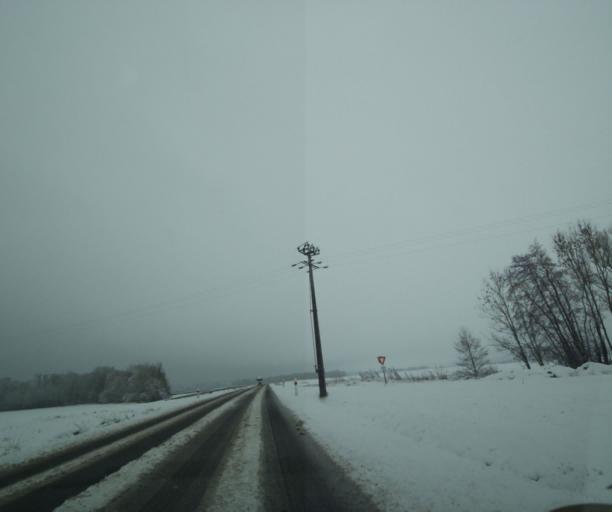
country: FR
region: Champagne-Ardenne
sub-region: Departement de la Haute-Marne
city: Saint-Dizier
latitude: 48.5706
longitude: 4.9173
